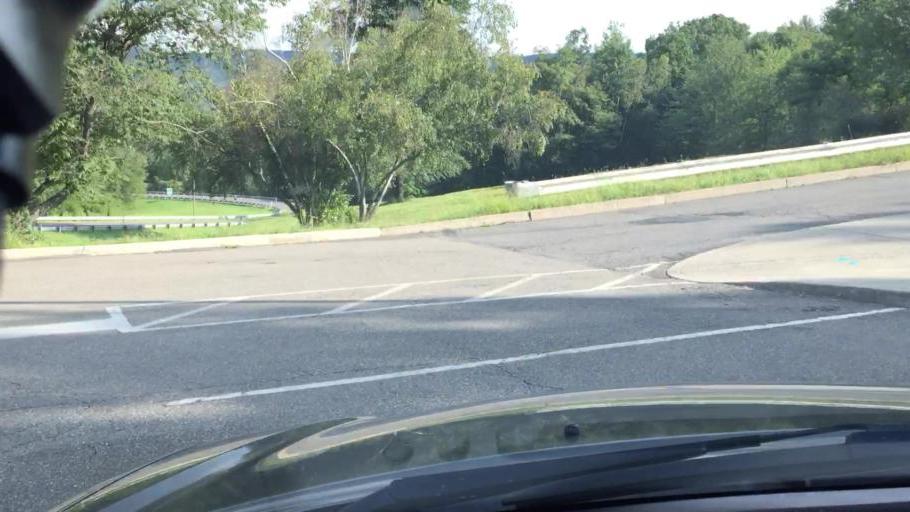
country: US
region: Pennsylvania
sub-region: Luzerne County
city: Nanticoke
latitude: 41.1957
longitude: -75.9899
